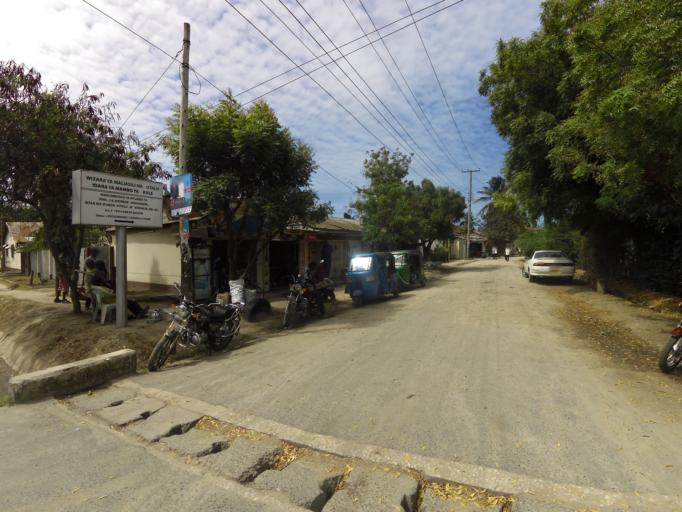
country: TZ
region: Dar es Salaam
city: Magomeni
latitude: -6.8082
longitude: 39.2524
